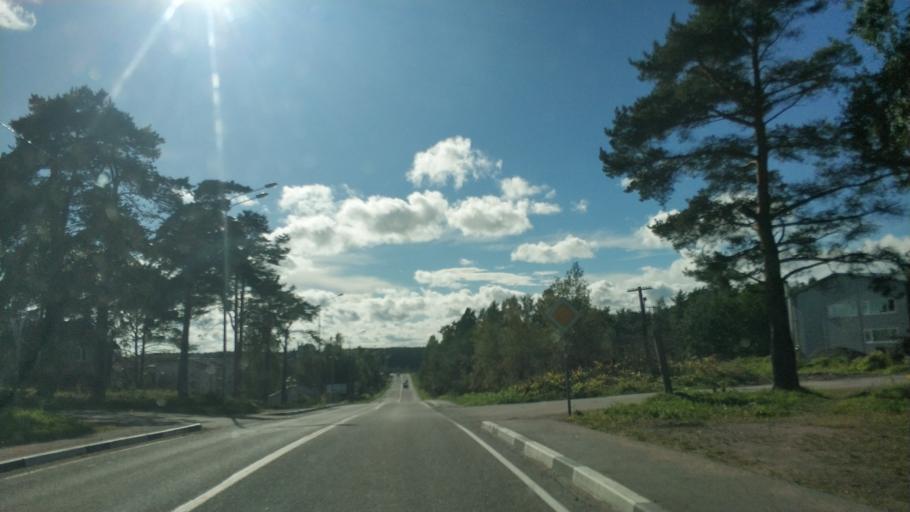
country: RU
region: Republic of Karelia
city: Khelyulya
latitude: 61.6490
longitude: 30.5946
